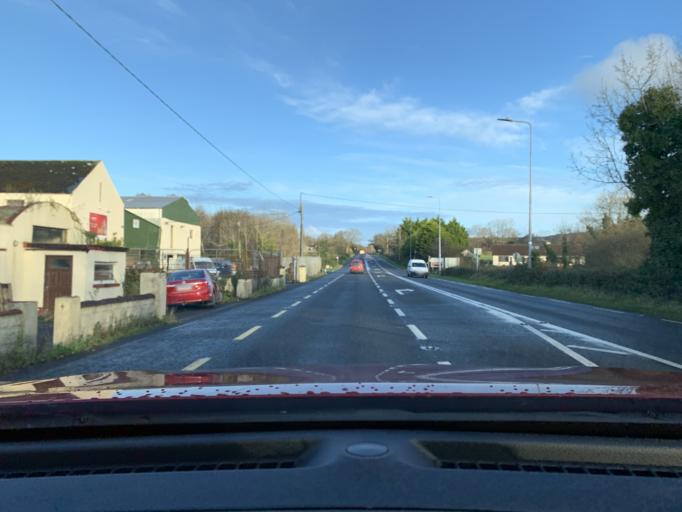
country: IE
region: Connaught
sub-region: Sligo
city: Sligo
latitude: 54.3408
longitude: -8.5029
